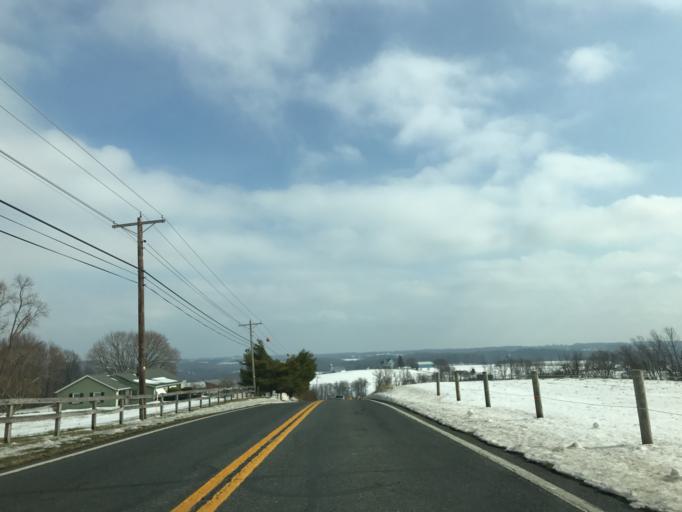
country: US
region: Maryland
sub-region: Harford County
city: South Bel Air
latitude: 39.6228
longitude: -76.2599
